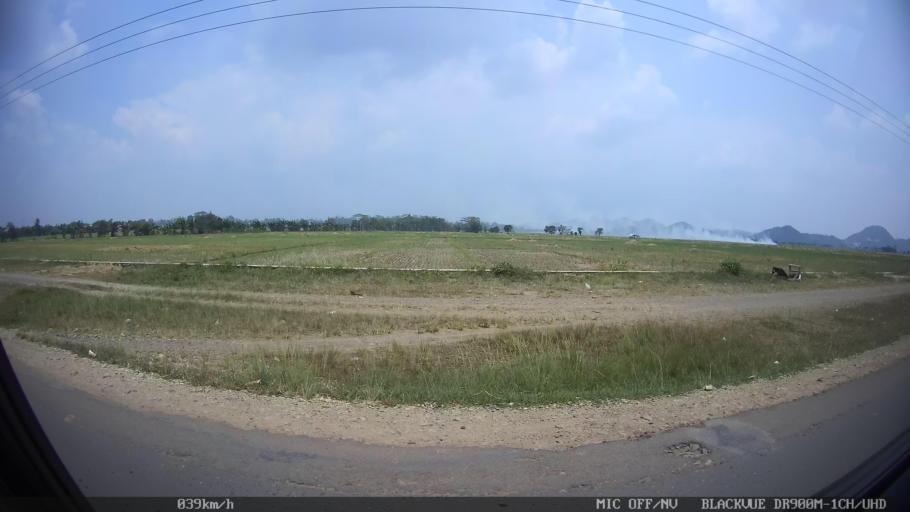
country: ID
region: Lampung
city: Pringsewu
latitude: -5.3547
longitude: 105.0126
